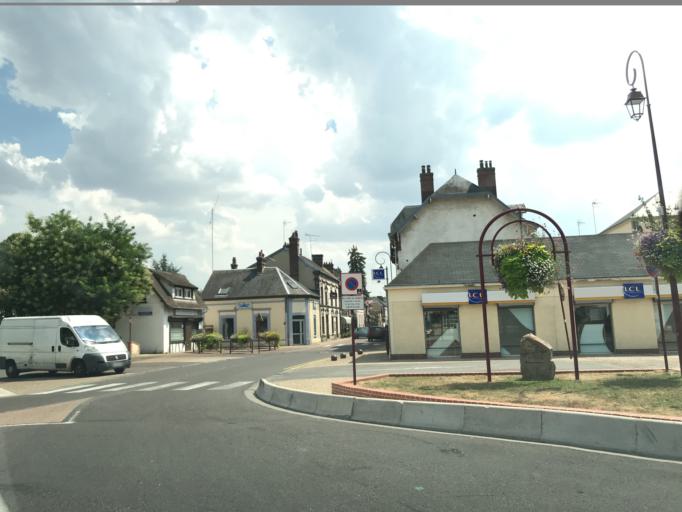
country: FR
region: Haute-Normandie
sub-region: Departement de l'Eure
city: Ezy-sur-Eure
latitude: 48.8659
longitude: 1.4199
